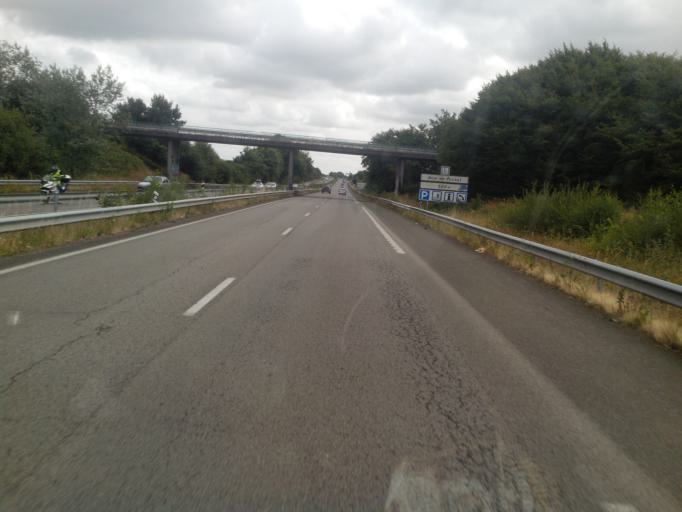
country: FR
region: Pays de la Loire
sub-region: Departement de la Loire-Atlantique
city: Nozay
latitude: 47.5440
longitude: -1.6353
